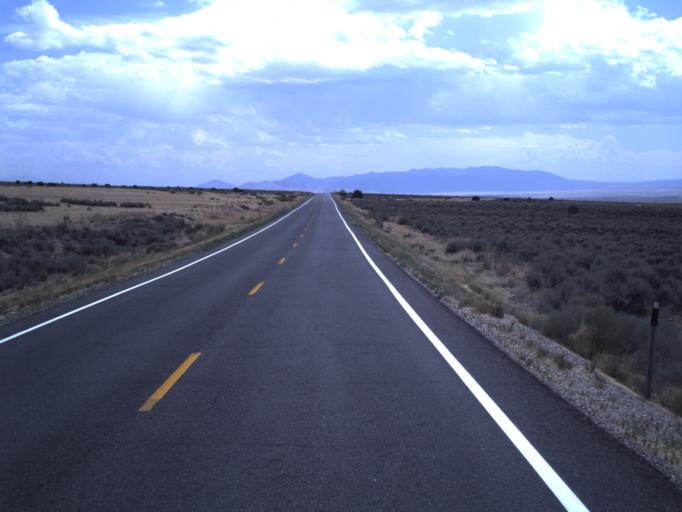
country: US
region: Utah
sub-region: Tooele County
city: Tooele
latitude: 40.3085
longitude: -112.2803
